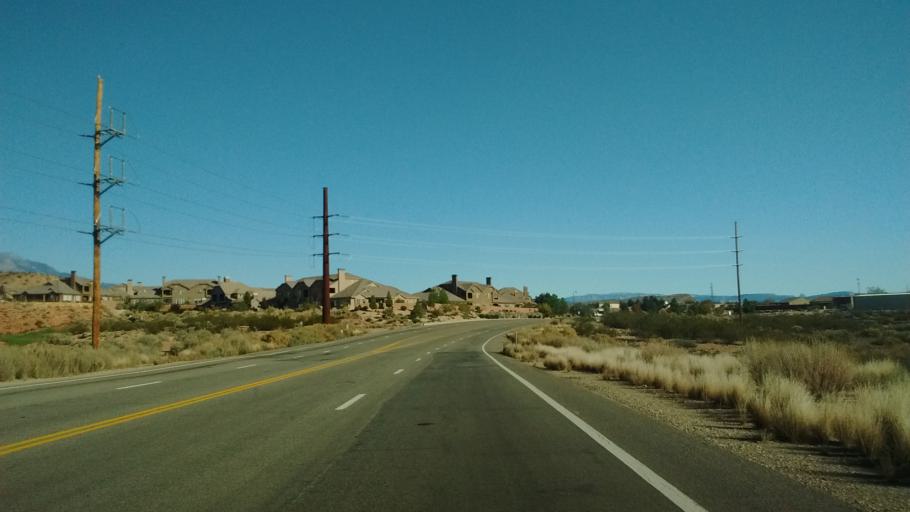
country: US
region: Utah
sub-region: Washington County
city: Washington
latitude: 37.1546
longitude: -113.4427
